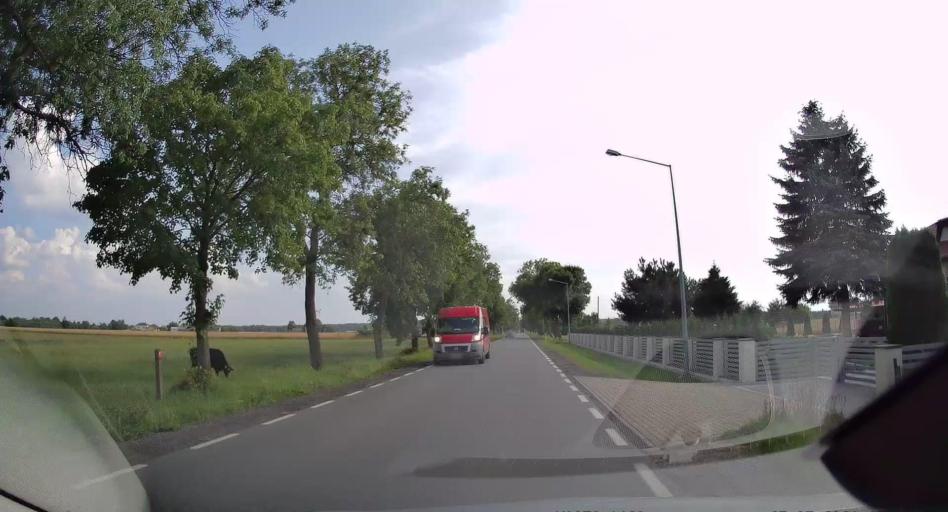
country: PL
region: Lodz Voivodeship
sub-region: Powiat tomaszowski
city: Rzeczyca
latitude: 51.5919
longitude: 20.2900
